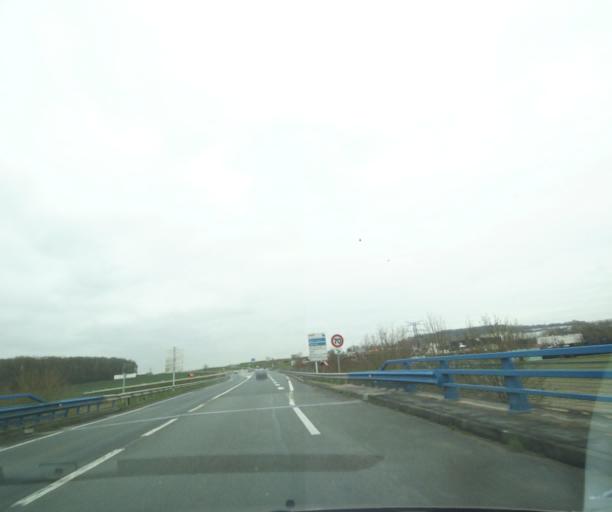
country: FR
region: Picardie
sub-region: Departement de l'Oise
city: Noyon
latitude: 49.5685
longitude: 2.9844
